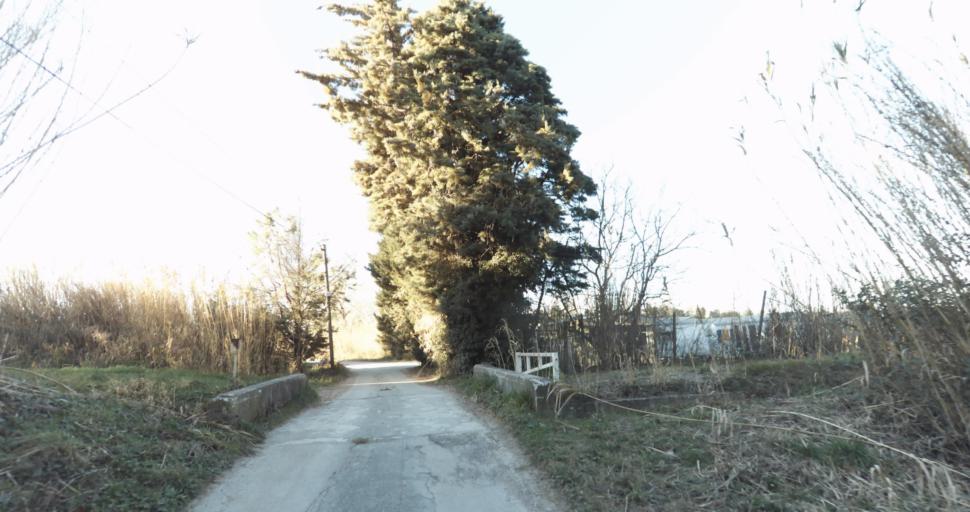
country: FR
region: Provence-Alpes-Cote d'Azur
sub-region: Departement des Bouches-du-Rhone
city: Barbentane
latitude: 43.9084
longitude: 4.7332
